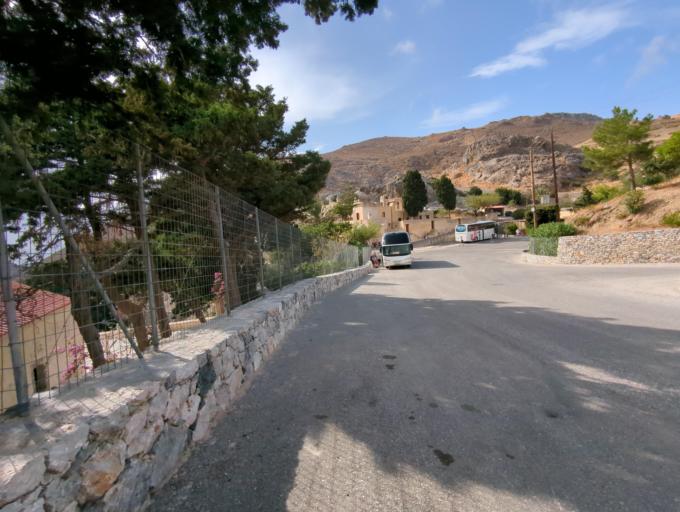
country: GR
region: Crete
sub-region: Nomos Rethymnis
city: Atsipopoulon
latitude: 35.1573
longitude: 24.4576
